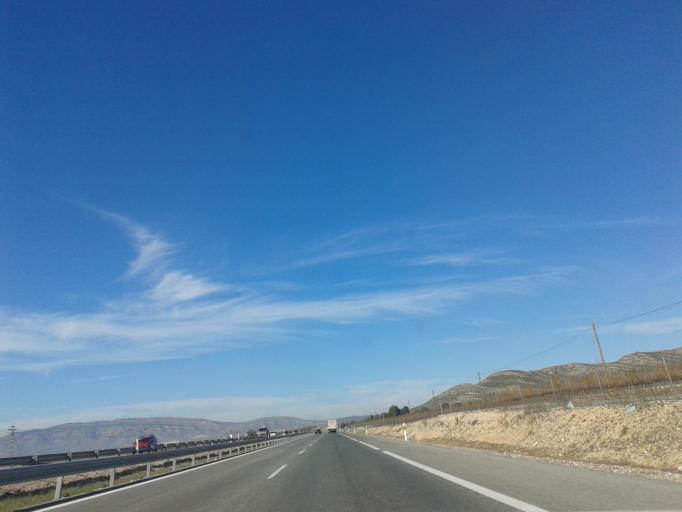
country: ES
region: Valencia
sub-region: Provincia de Alicante
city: Villena
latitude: 38.6836
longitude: -0.9015
